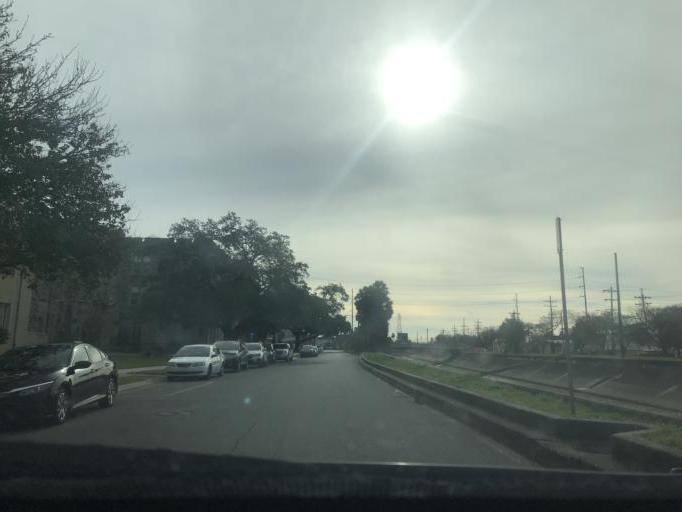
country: US
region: Louisiana
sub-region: Orleans Parish
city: New Orleans
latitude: 29.9646
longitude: -90.1082
